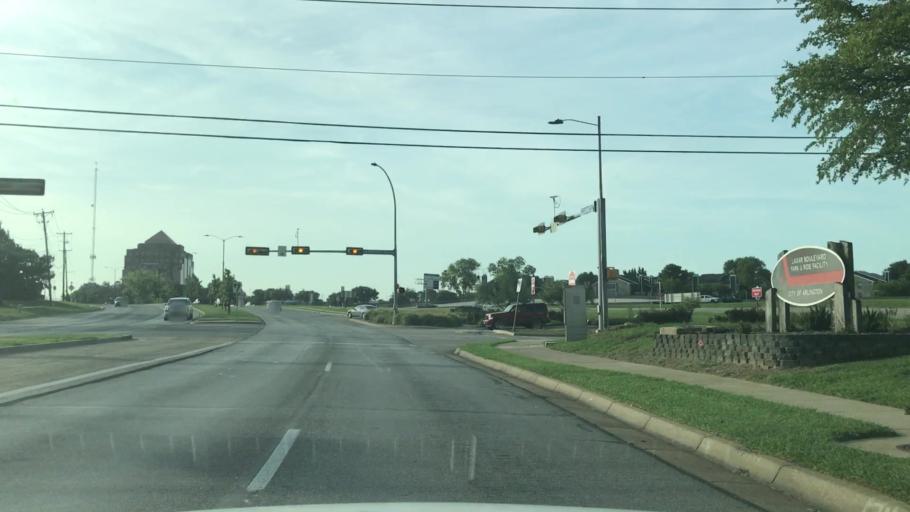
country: US
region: Texas
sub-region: Tarrant County
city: Arlington
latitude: 32.7615
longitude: -97.1188
